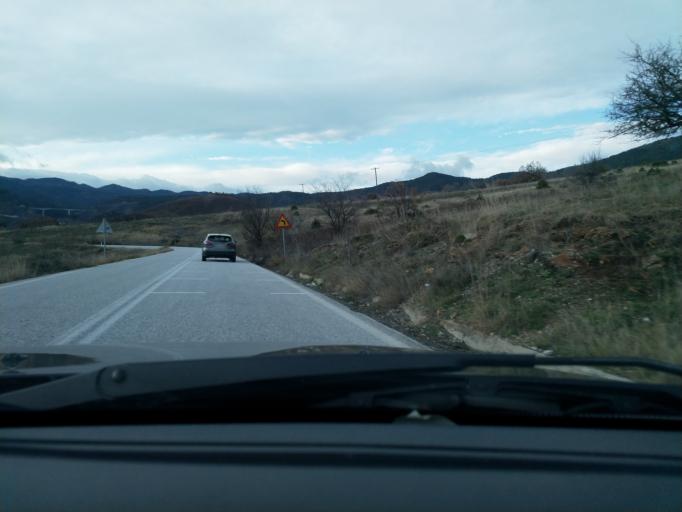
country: GR
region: Epirus
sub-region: Nomos Ioanninon
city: Metsovo
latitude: 39.7963
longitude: 21.3653
